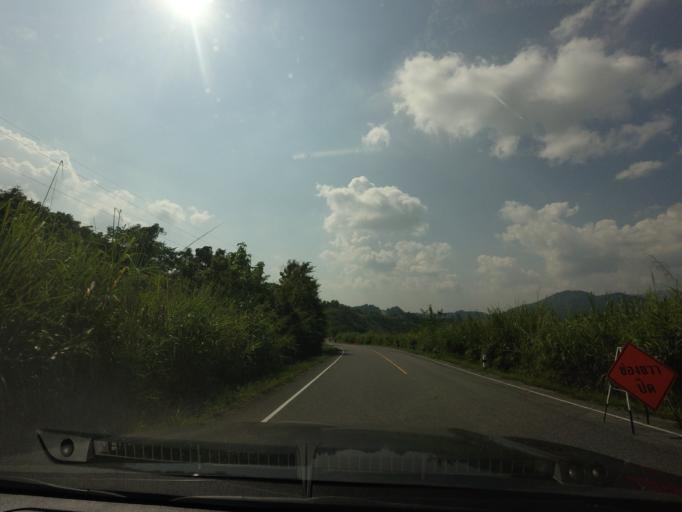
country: TH
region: Nan
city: Santi Suk
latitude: 18.9727
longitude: 101.0250
